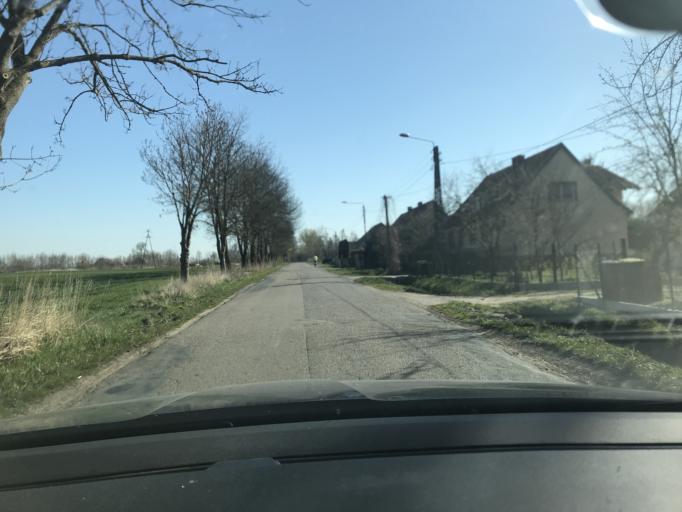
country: PL
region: Pomeranian Voivodeship
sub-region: Powiat nowodworski
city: Sztutowo
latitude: 54.3145
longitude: 19.1598
